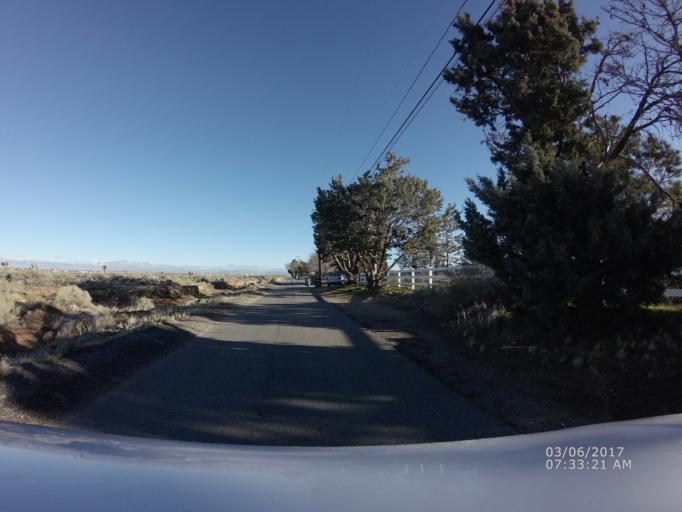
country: US
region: California
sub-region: Los Angeles County
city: Quartz Hill
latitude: 34.6694
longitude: -118.2232
